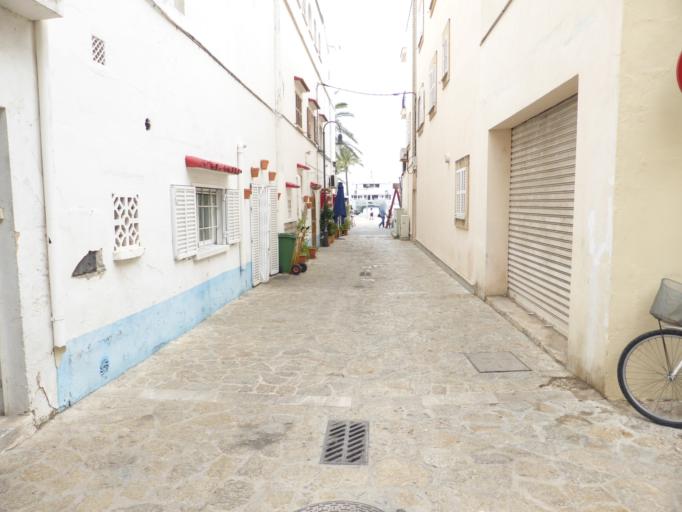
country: ES
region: Balearic Islands
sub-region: Illes Balears
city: Port d'Alcudia
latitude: 39.8417
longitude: 3.1356
